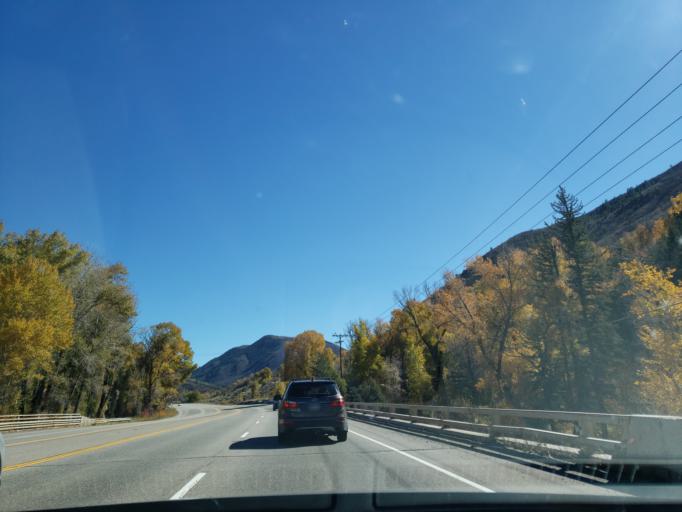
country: US
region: Colorado
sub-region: Eagle County
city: Basalt
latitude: 39.3429
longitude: -107.0066
